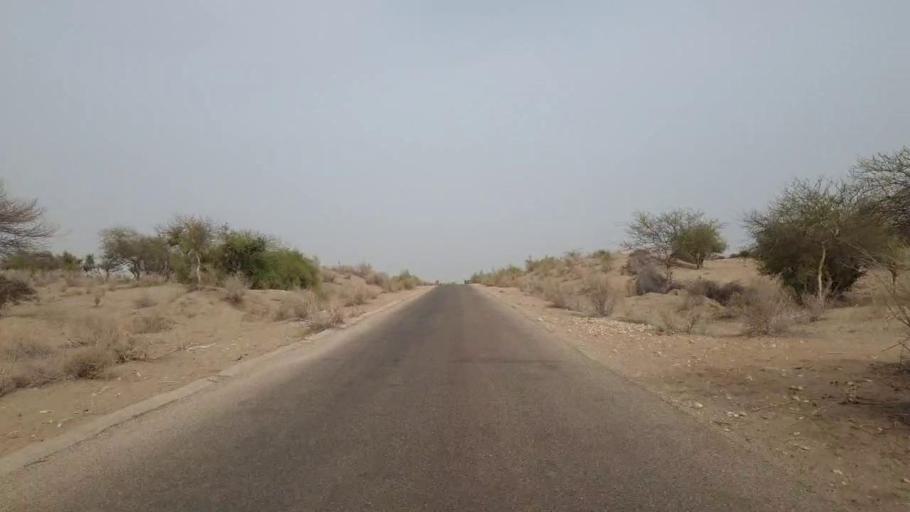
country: PK
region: Sindh
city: Islamkot
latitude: 24.5592
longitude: 70.3432
